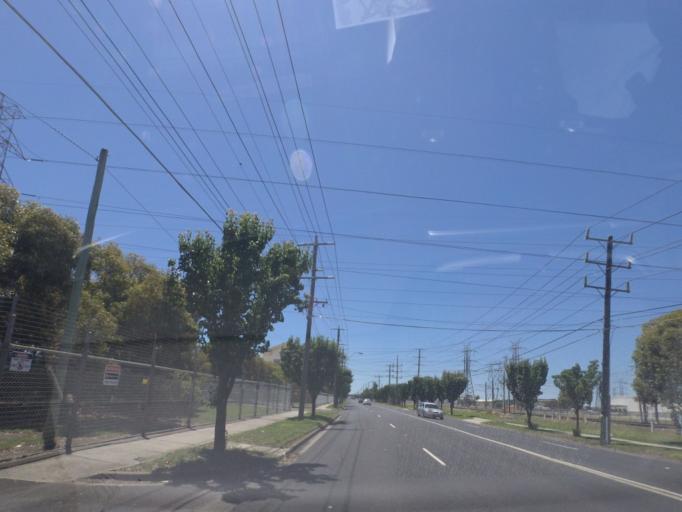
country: AU
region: Victoria
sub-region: Whittlesea
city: Thomastown
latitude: -37.6933
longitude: 145.0116
